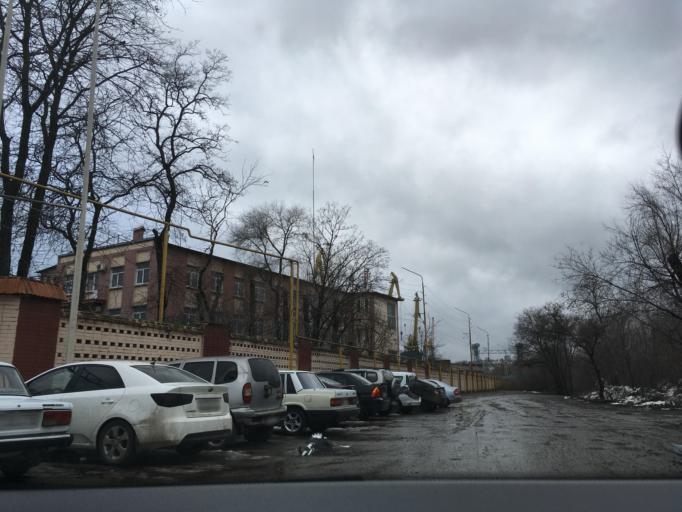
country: RU
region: Rostov
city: Rostov-na-Donu
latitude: 47.2111
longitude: 39.7146
